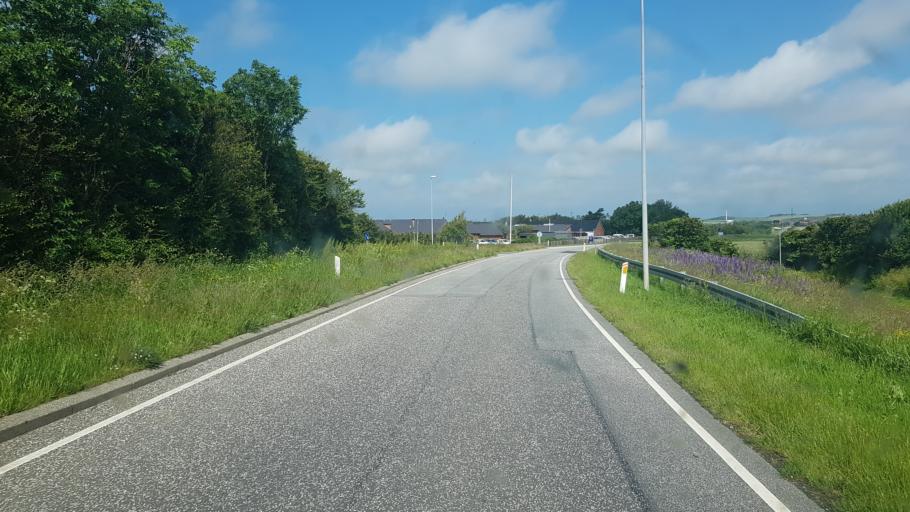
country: DK
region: Central Jutland
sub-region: Lemvig Kommune
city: Lemvig
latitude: 56.5543
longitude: 8.2336
